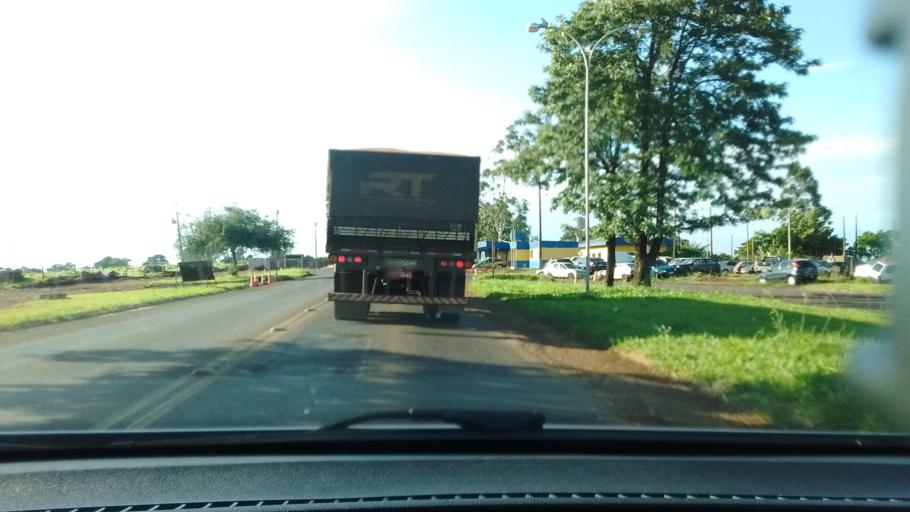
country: BR
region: Parana
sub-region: Cascavel
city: Cascavel
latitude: -25.1823
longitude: -53.6018
